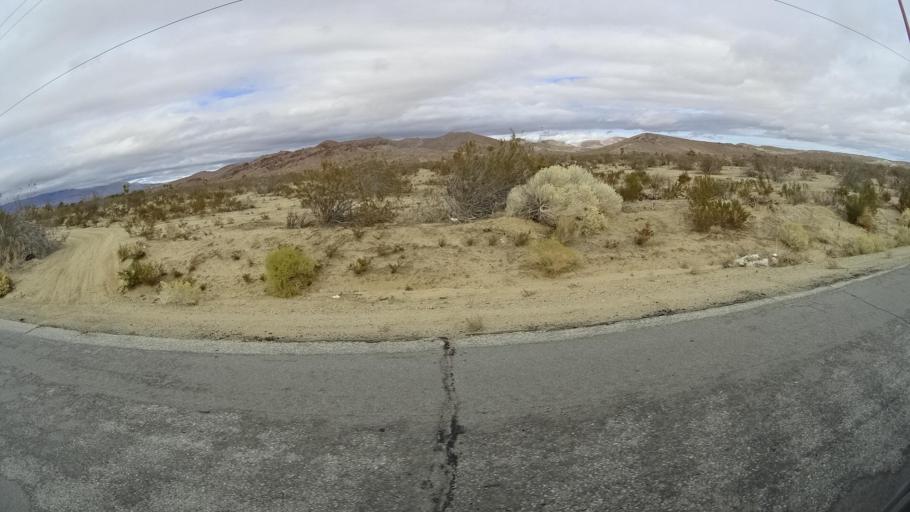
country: US
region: California
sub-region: Kern County
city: Rosamond
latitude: 34.8928
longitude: -118.2316
